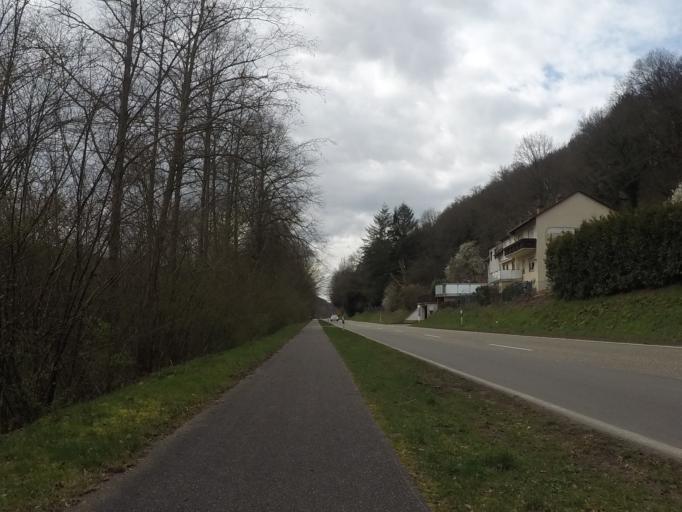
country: DE
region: Rheinland-Pfalz
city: Hohfroschen
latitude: 49.2616
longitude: 7.5599
